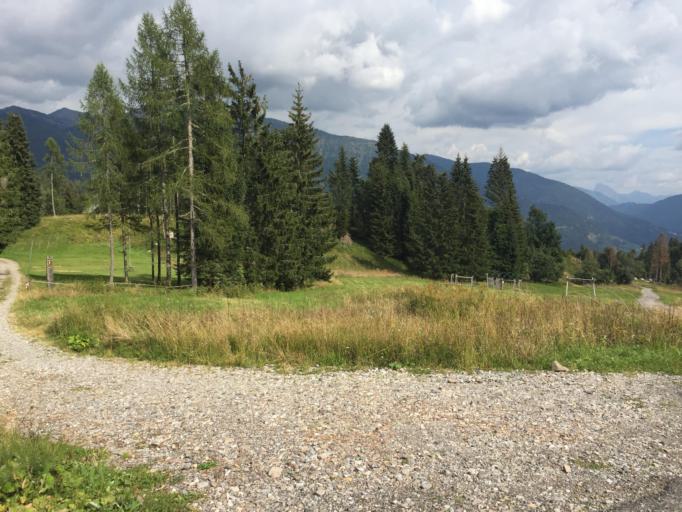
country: IT
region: Friuli Venezia Giulia
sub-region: Provincia di Udine
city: Rigolato
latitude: 46.5546
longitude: 12.8122
